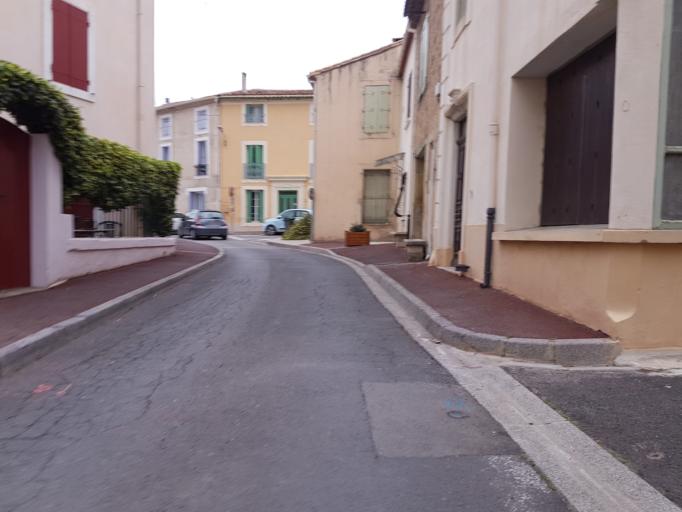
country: FR
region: Languedoc-Roussillon
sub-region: Departement de l'Herault
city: Cers
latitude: 43.3242
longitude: 3.3056
